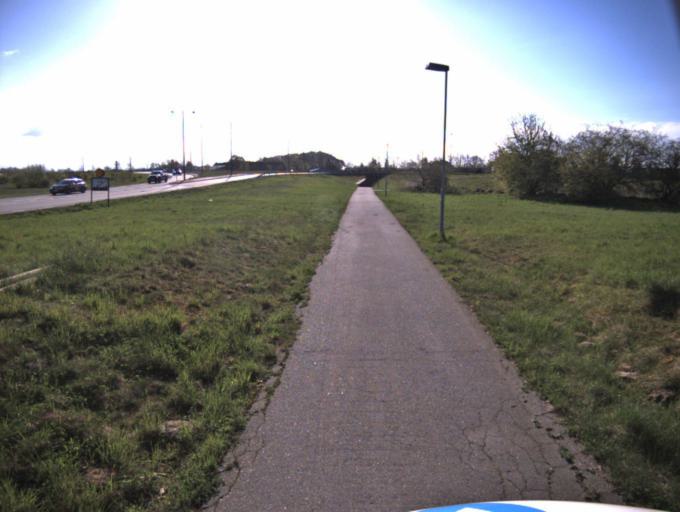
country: SE
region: Skane
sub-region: Kristianstads Kommun
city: Norra Asum
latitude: 56.0020
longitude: 14.0990
